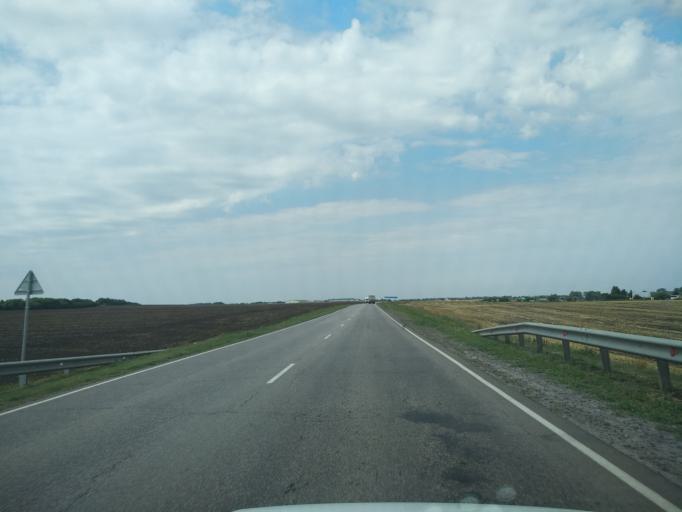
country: RU
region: Voronezj
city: Verkhnyaya Khava
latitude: 51.6814
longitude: 39.9000
